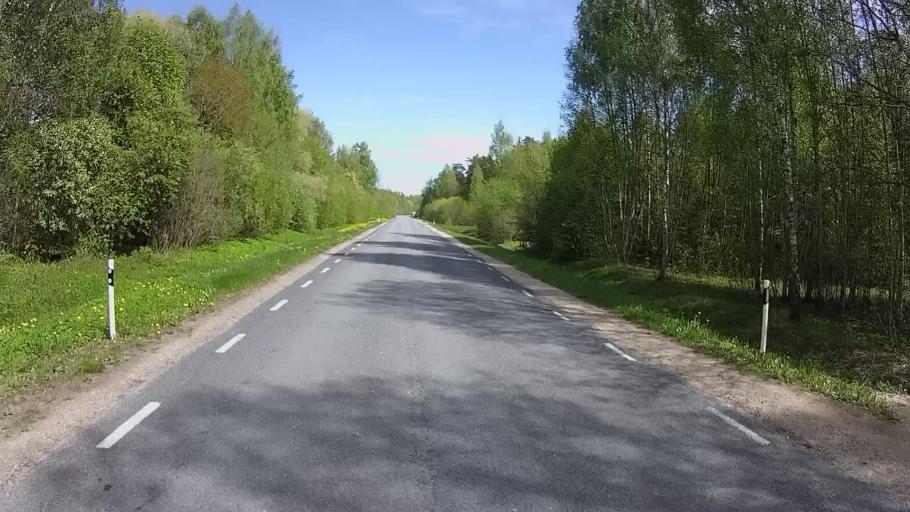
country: LV
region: Apes Novads
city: Ape
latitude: 57.6042
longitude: 26.5272
